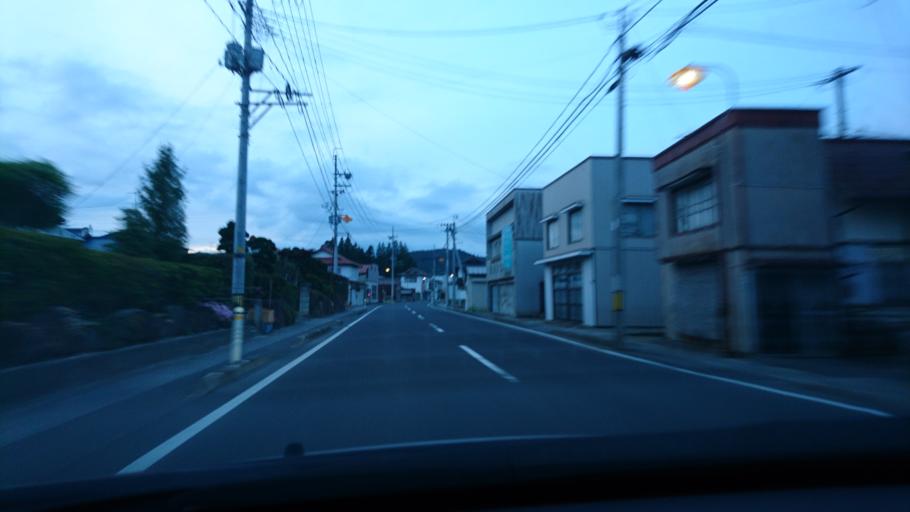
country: JP
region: Iwate
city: Ichinoseki
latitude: 38.8261
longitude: 140.9856
